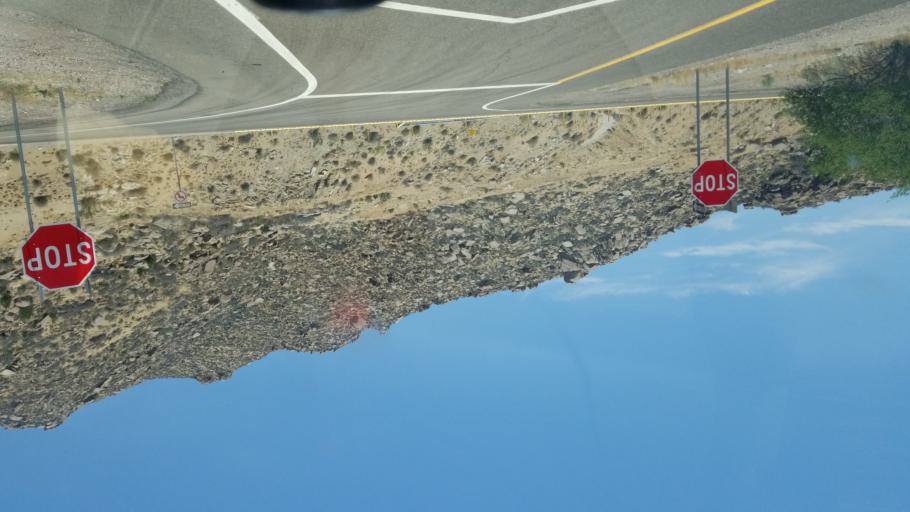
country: US
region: New Mexico
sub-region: Bernalillo County
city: Carnuel
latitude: 35.0631
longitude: -106.4659
